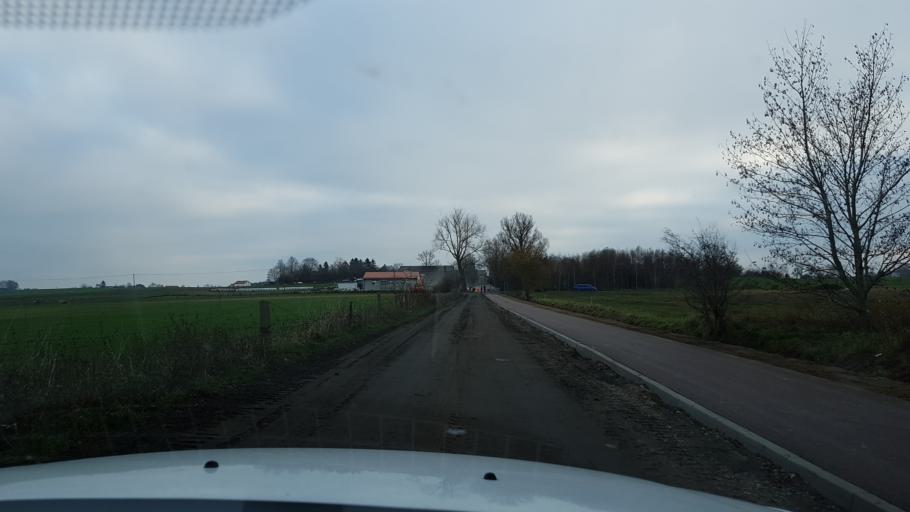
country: PL
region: West Pomeranian Voivodeship
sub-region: Powiat kolobrzeski
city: Grzybowo
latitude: 54.1234
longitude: 15.5199
